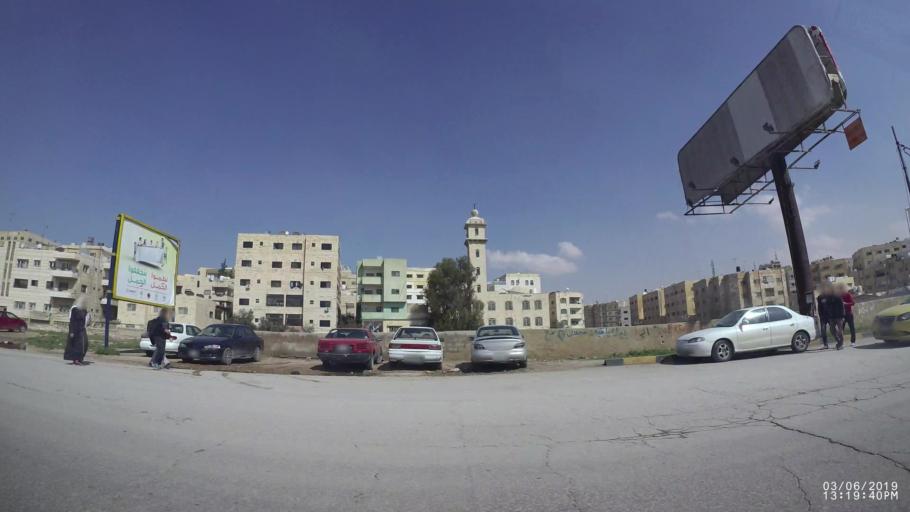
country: JO
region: Zarqa
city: Zarqa
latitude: 32.0435
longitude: 36.0940
